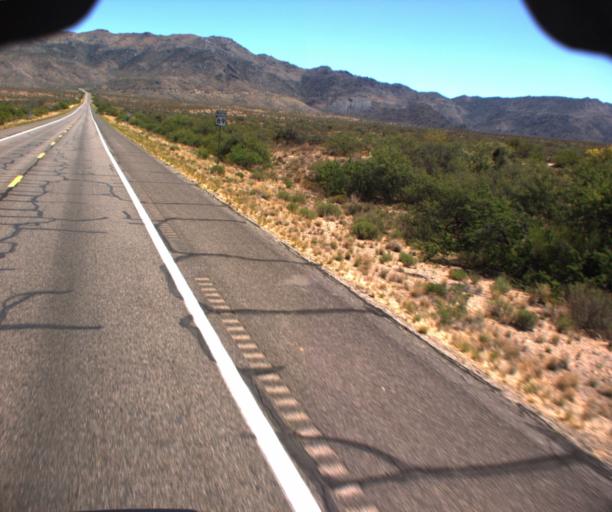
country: US
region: Arizona
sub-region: Yavapai County
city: Congress
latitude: 34.1836
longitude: -112.8247
